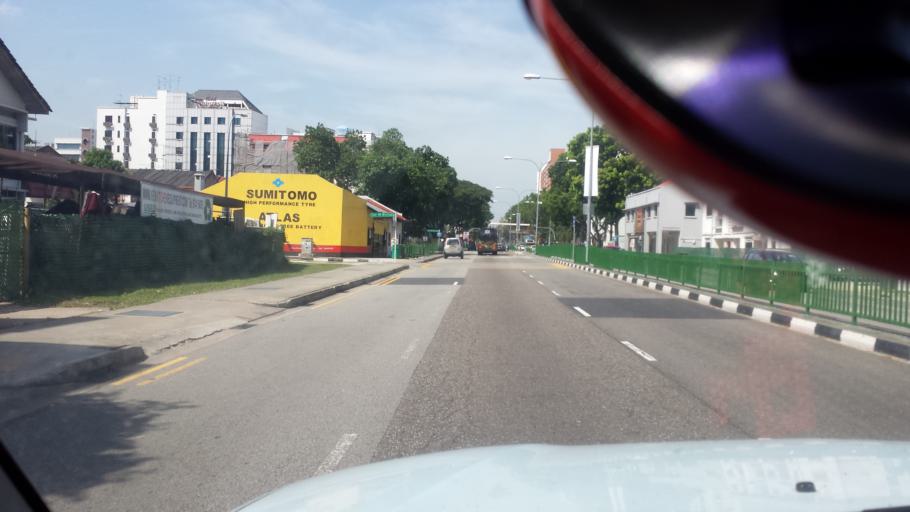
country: SG
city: Singapore
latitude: 1.3101
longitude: 103.8801
